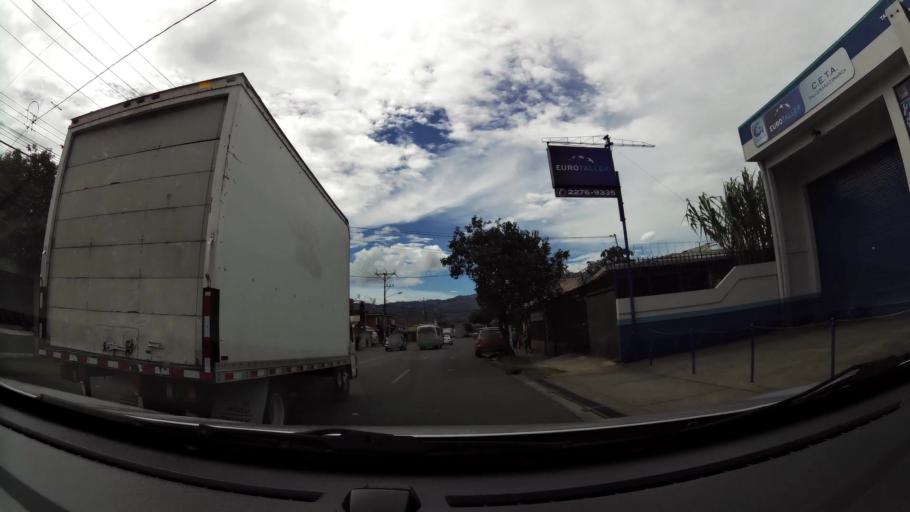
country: CR
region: San Jose
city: Curridabat
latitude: 9.9010
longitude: -84.0462
